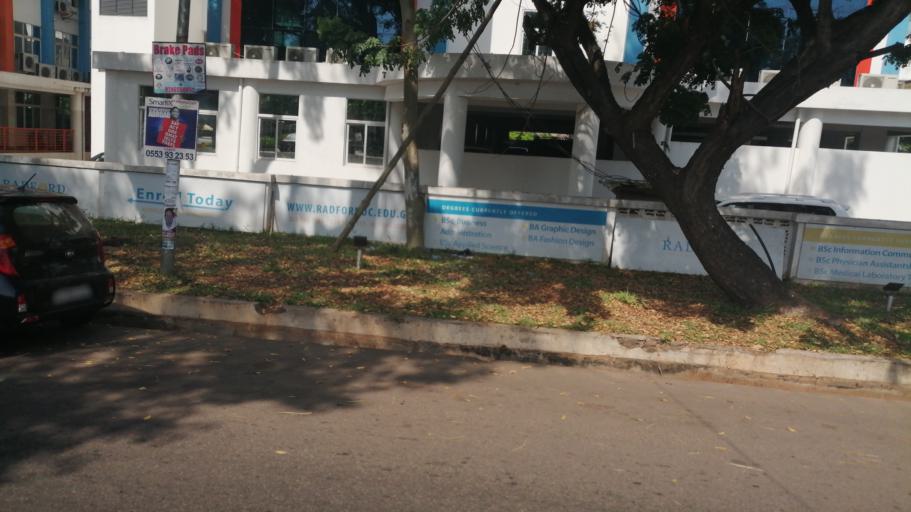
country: GH
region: Greater Accra
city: Medina Estates
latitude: 5.6380
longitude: -0.1713
